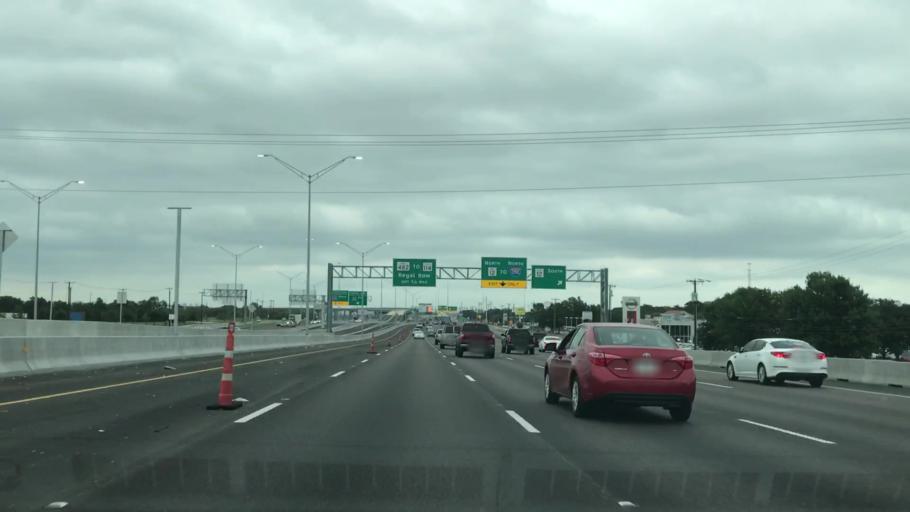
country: US
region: Texas
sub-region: Dallas County
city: Irving
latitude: 32.8368
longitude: -96.9289
